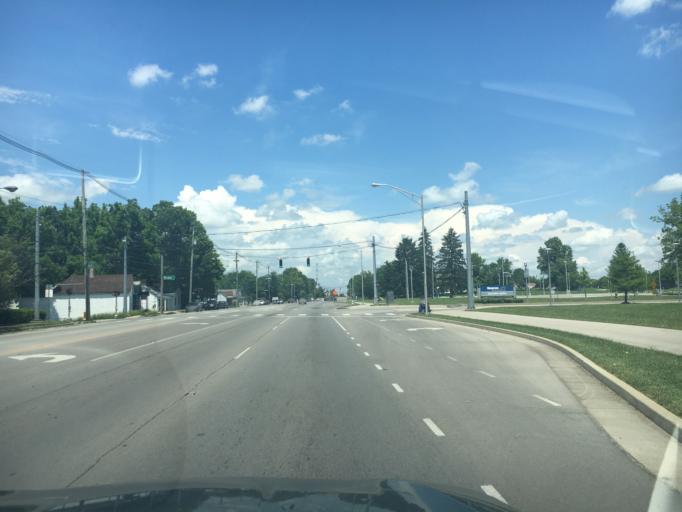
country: US
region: Kentucky
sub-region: Fayette County
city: Mount Vernon
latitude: 38.0612
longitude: -84.5005
